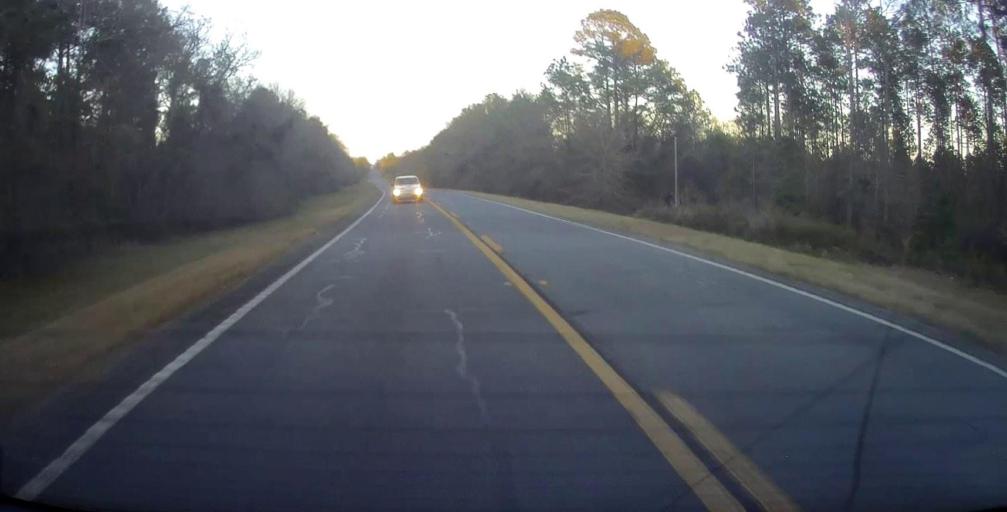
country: US
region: Georgia
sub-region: Dodge County
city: Eastman
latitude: 32.2667
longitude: -83.1267
